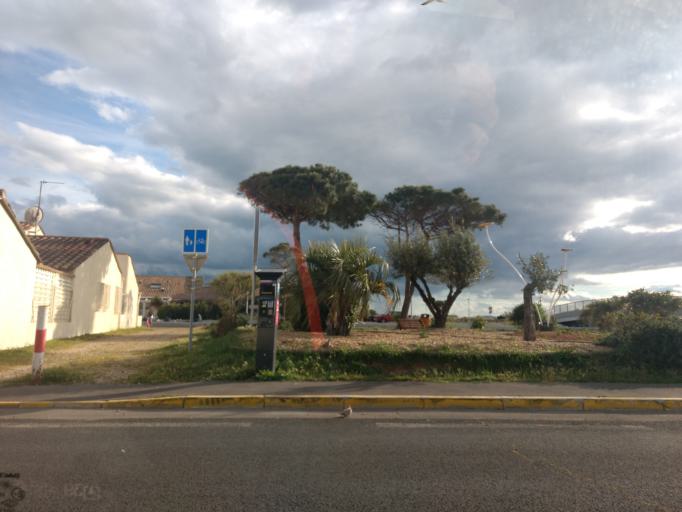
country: FR
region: Languedoc-Roussillon
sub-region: Departement de l'Herault
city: Palavas-les-Flots
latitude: 43.5268
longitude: 3.9207
